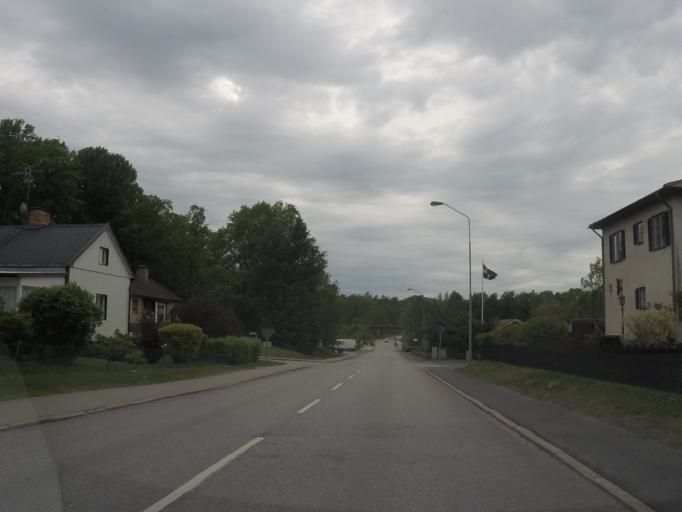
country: SE
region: Soedermanland
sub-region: Flens Kommun
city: Malmkoping
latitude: 59.0706
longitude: 16.8296
